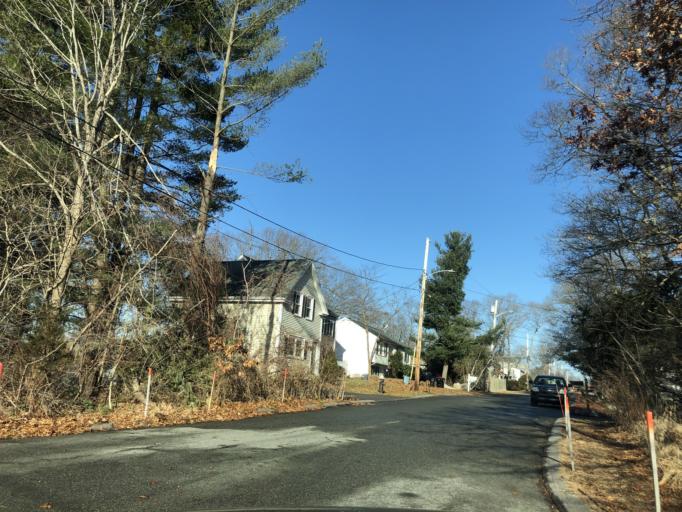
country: US
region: Massachusetts
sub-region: Plymouth County
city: Brockton
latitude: 42.0991
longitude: -71.0049
